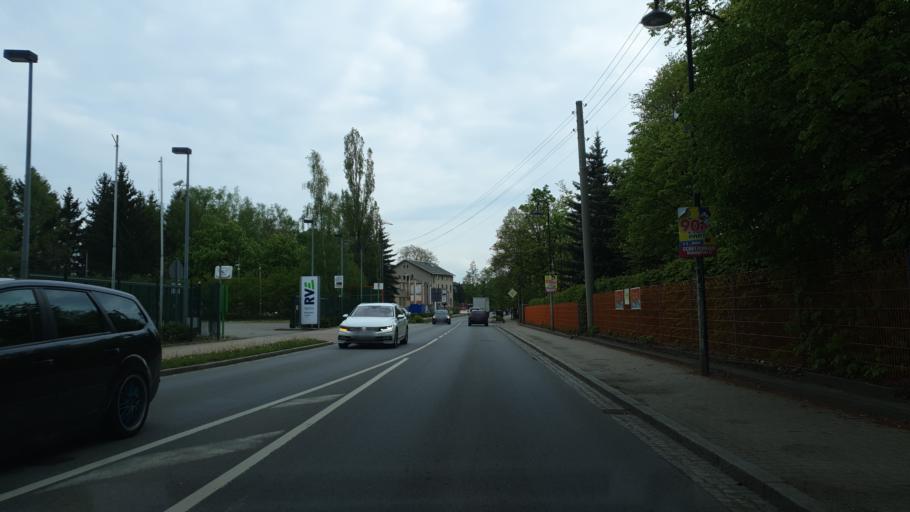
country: DE
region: Saxony
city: Lugau
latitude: 50.7418
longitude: 12.7468
